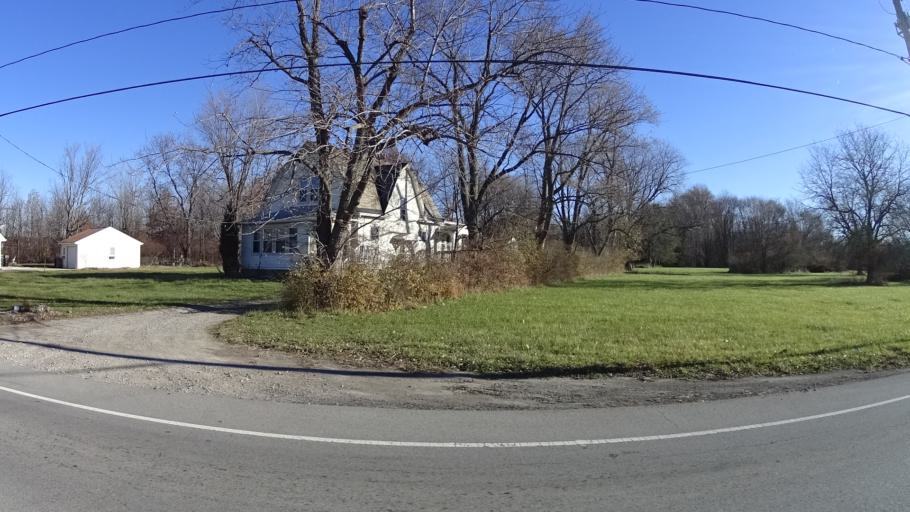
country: US
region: Ohio
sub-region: Lorain County
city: Sheffield
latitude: 41.4024
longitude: -82.1086
